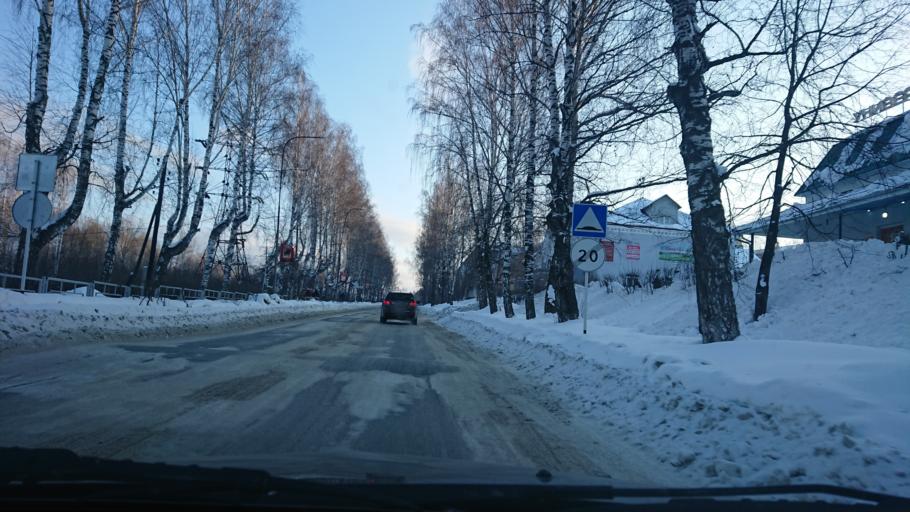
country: RU
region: Sverdlovsk
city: Degtyarsk
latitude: 56.6956
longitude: 60.0885
